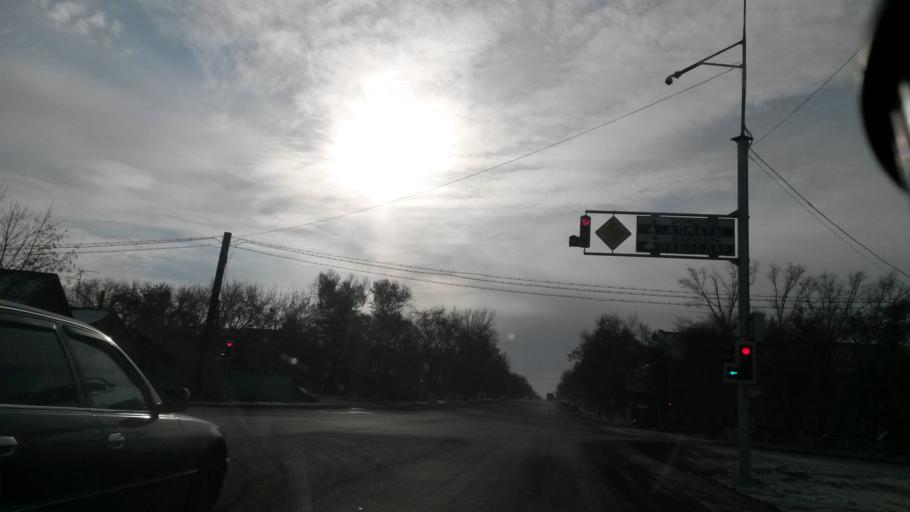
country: KZ
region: Qaraghandy
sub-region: Qaraghandy Qalasy
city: Karagandy
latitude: 49.8240
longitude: 73.0937
